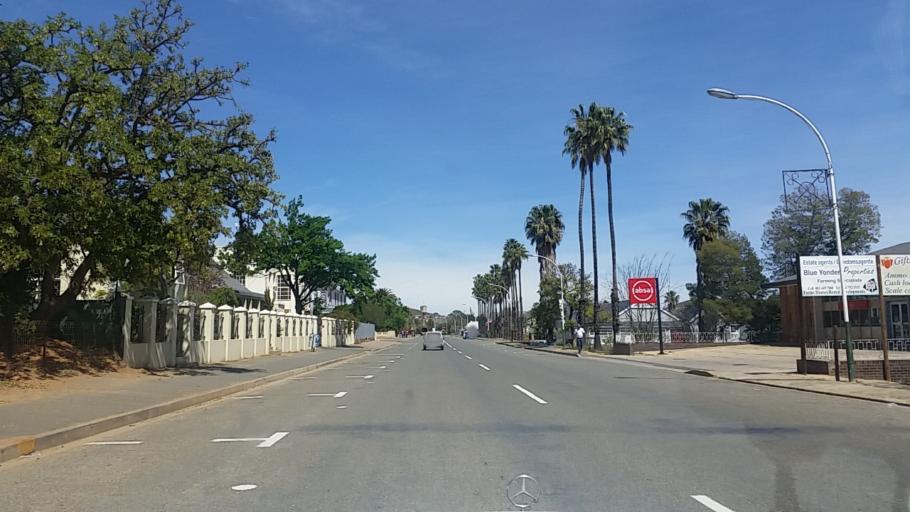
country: ZA
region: Western Cape
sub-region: Eden District Municipality
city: Knysna
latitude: -33.6558
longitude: 23.1281
